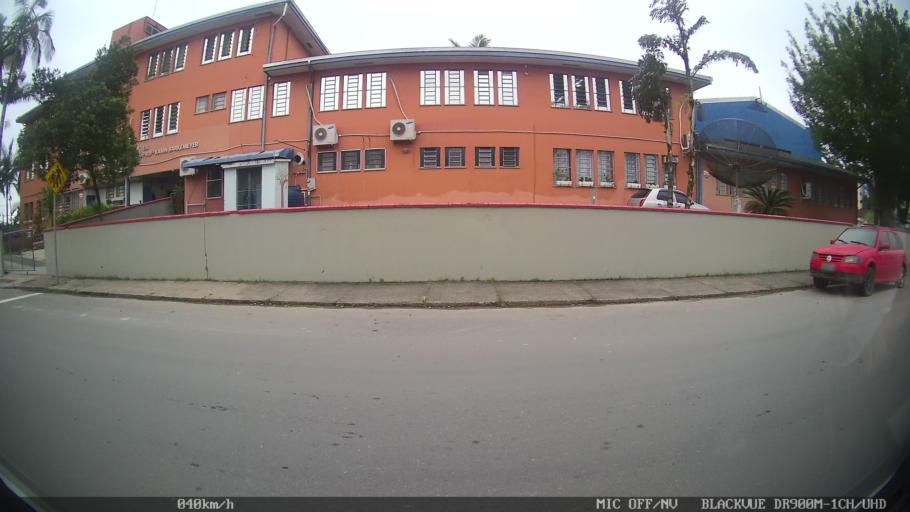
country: BR
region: Santa Catarina
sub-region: Joinville
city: Joinville
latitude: -26.2923
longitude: -48.9098
